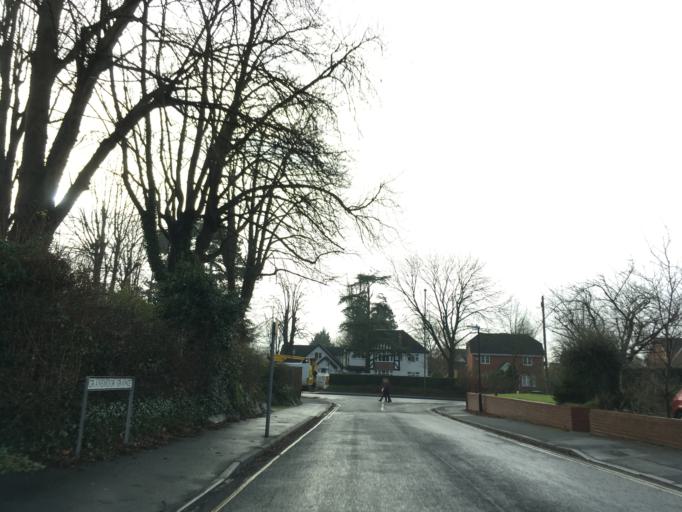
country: GB
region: England
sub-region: Gloucestershire
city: Barnwood
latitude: 51.8528
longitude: -2.1781
